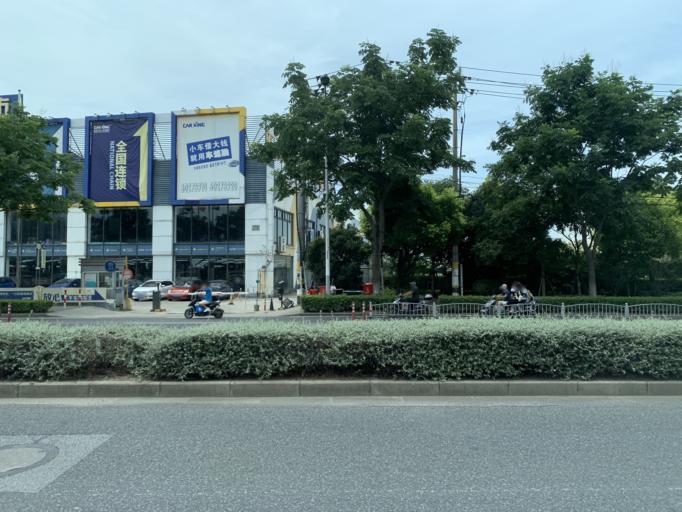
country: CN
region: Shanghai Shi
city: Kangqiao
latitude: 31.1576
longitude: 121.5602
